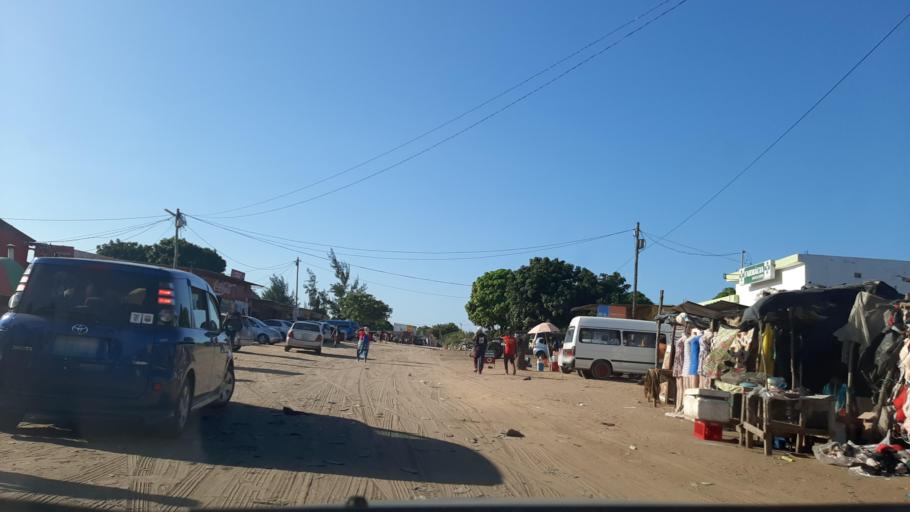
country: MZ
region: Maputo City
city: Maputo
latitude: -25.8101
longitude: 32.5463
